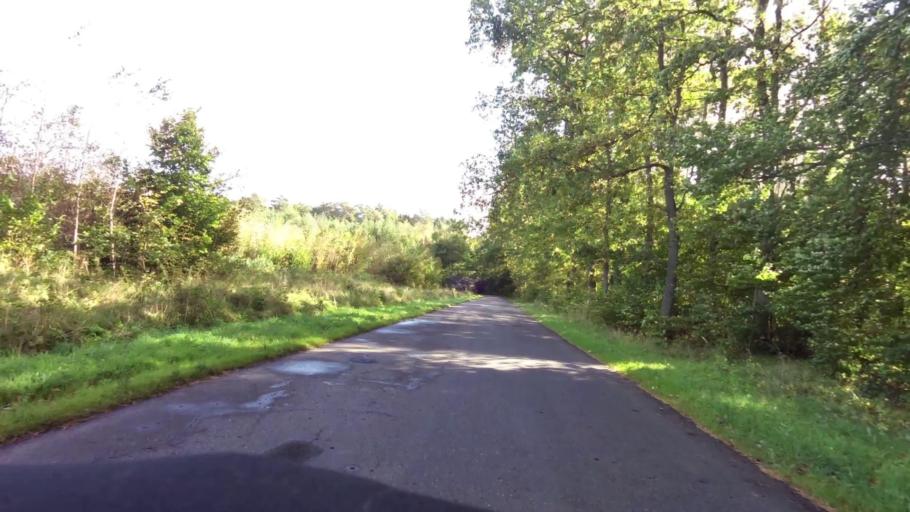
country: PL
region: West Pomeranian Voivodeship
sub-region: Powiat bialogardzki
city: Bialogard
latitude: 53.9936
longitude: 16.0929
